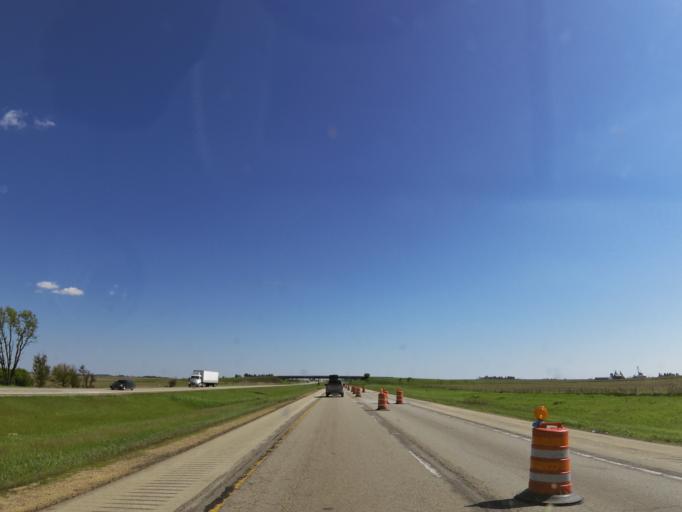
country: US
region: Illinois
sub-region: Ogle County
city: Hillcrest
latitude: 42.0257
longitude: -89.0212
